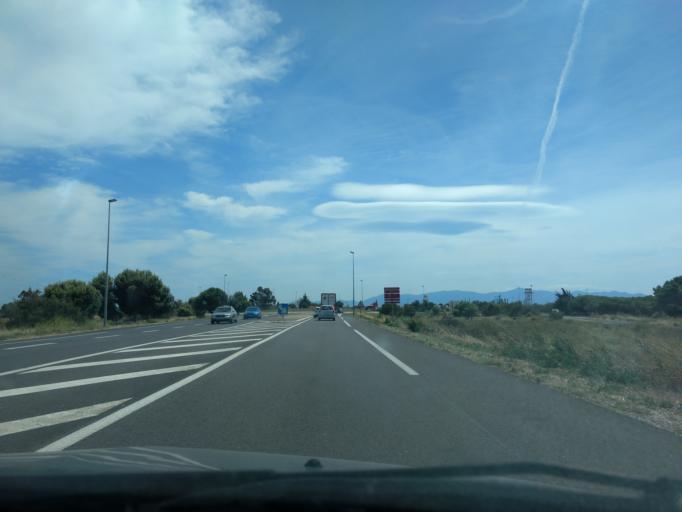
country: FR
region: Languedoc-Roussillon
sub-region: Departement des Pyrenees-Orientales
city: Torreilles
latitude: 42.7640
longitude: 3.0189
